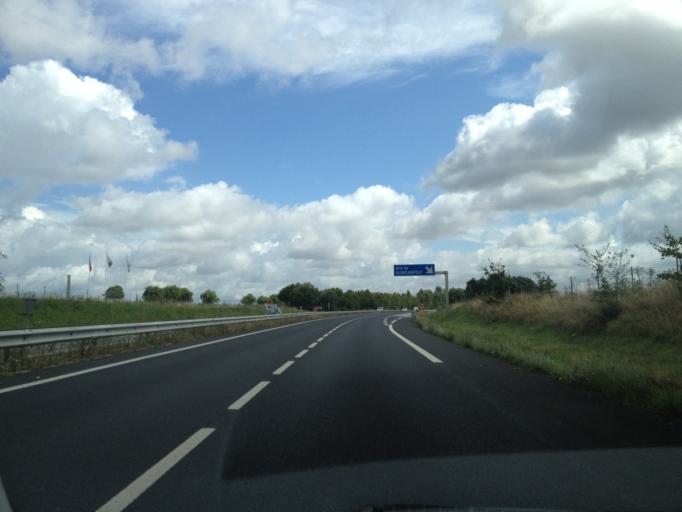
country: FR
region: Haute-Normandie
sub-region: Departement de la Seine-Maritime
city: Quincampoix
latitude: 49.5289
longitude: 1.2044
